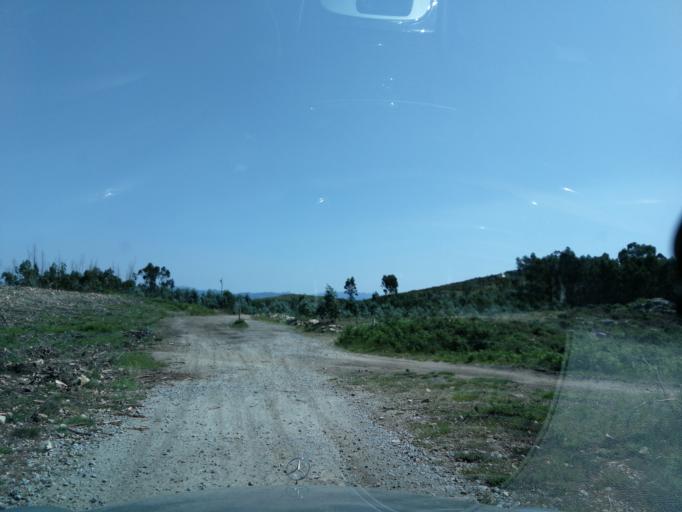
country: PT
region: Braga
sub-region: Povoa de Lanhoso
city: Povoa de Lanhoso
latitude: 41.5677
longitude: -8.3370
